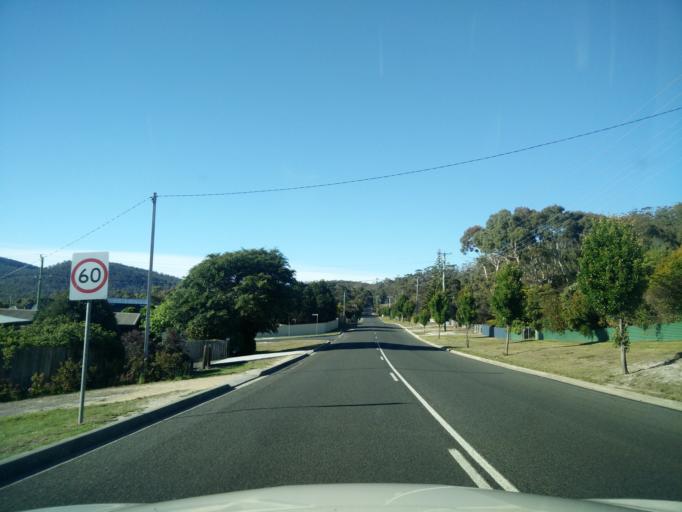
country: AU
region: Tasmania
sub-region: Break O'Day
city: St Helens
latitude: -41.8796
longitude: 148.3030
